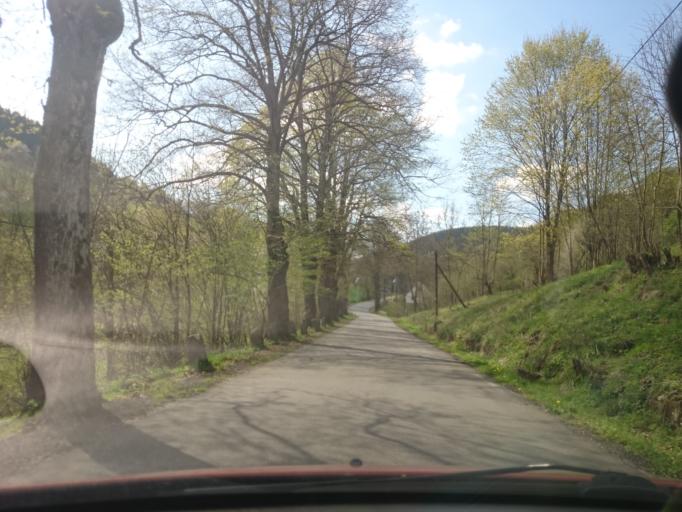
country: PL
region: Lower Silesian Voivodeship
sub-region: Powiat klodzki
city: Bystrzyca Klodzka
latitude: 50.3012
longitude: 16.5407
